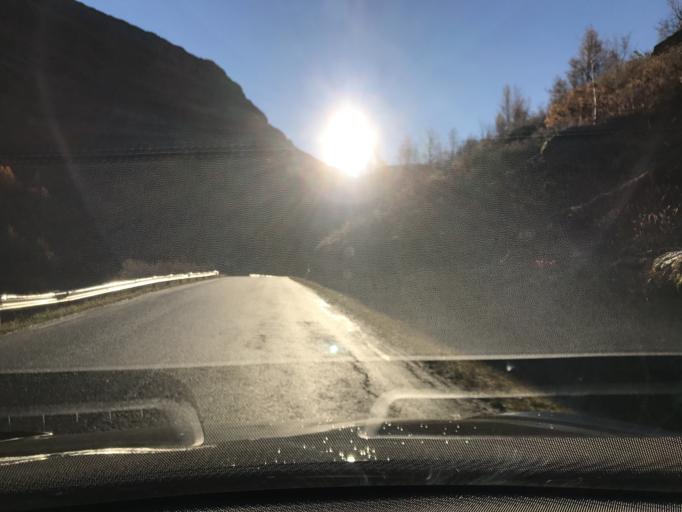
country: NO
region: Sogn og Fjordane
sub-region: Laerdal
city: Laerdalsoyri
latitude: 60.8137
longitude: 7.5522
